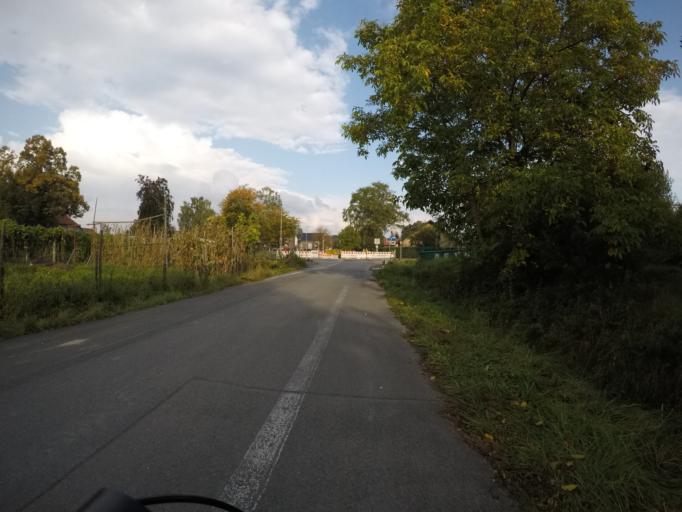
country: DE
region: North Rhine-Westphalia
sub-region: Regierungsbezirk Detmold
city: Bielefeld
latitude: 52.0419
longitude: 8.5896
